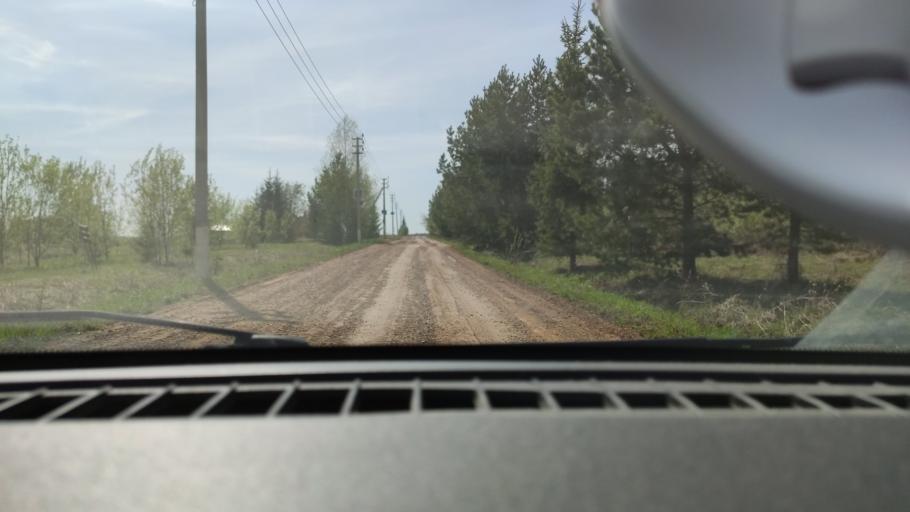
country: RU
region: Perm
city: Kultayevo
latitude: 57.8853
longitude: 55.8541
